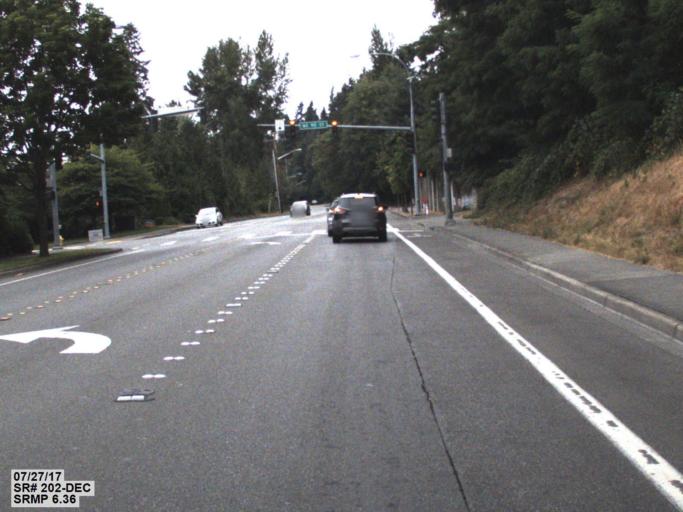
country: US
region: Washington
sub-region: King County
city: Redmond
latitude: 47.6824
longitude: -122.1234
